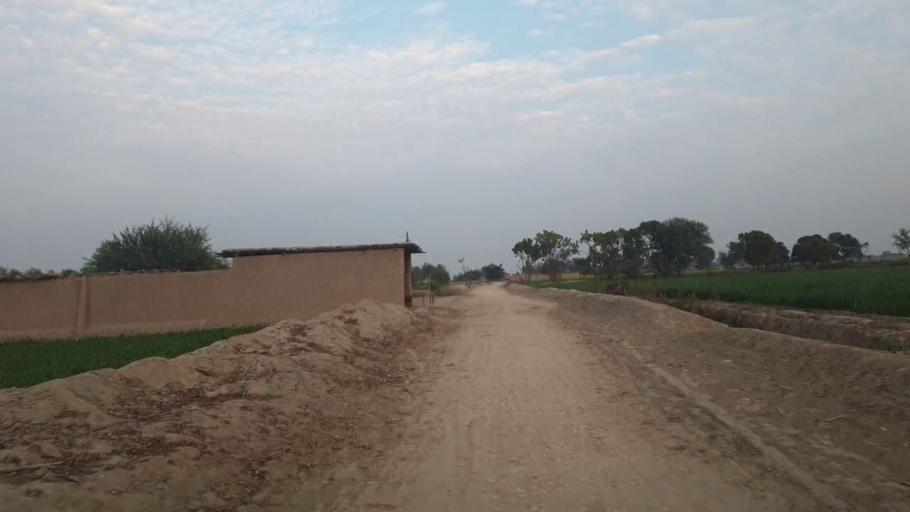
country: PK
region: Sindh
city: Shahpur Chakar
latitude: 26.0875
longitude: 68.5522
